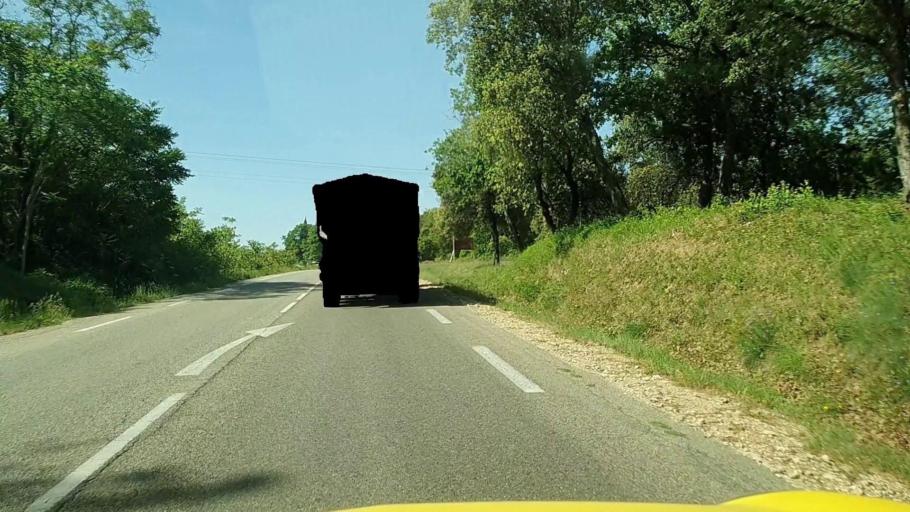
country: FR
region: Languedoc-Roussillon
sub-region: Departement du Gard
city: Connaux
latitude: 44.0601
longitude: 4.5711
